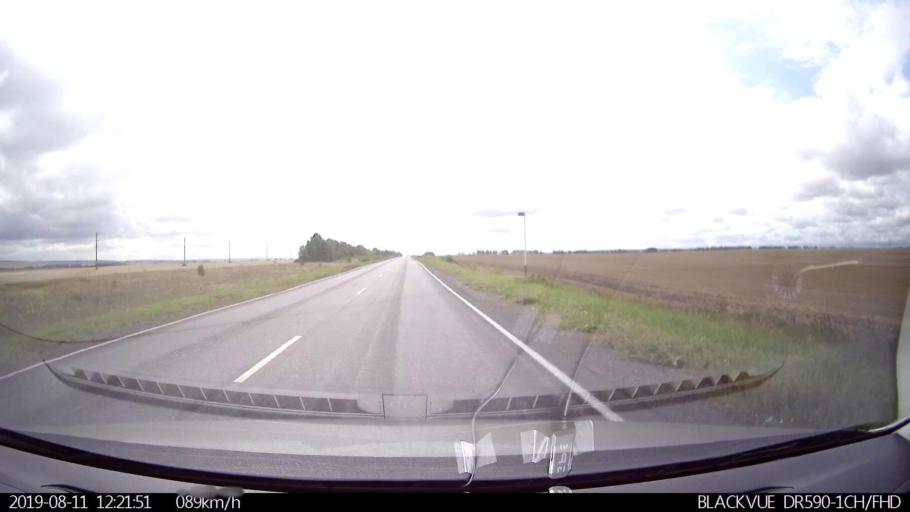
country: RU
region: Ulyanovsk
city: Ignatovka
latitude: 53.9159
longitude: 47.9563
